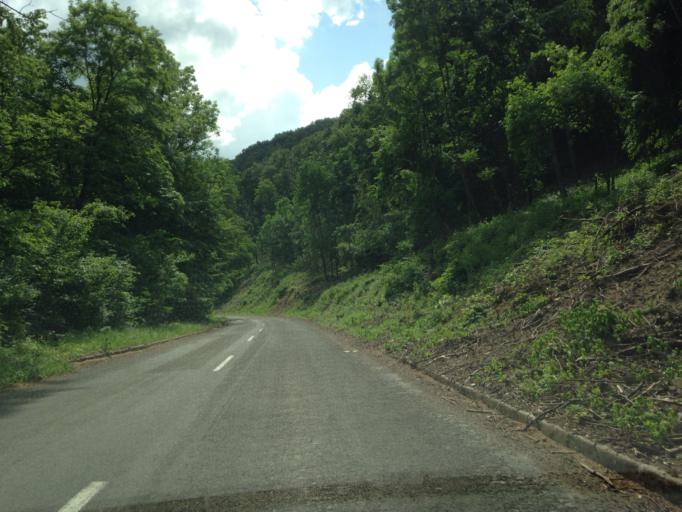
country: HU
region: Pest
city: Visegrad
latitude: 47.7500
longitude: 18.9423
